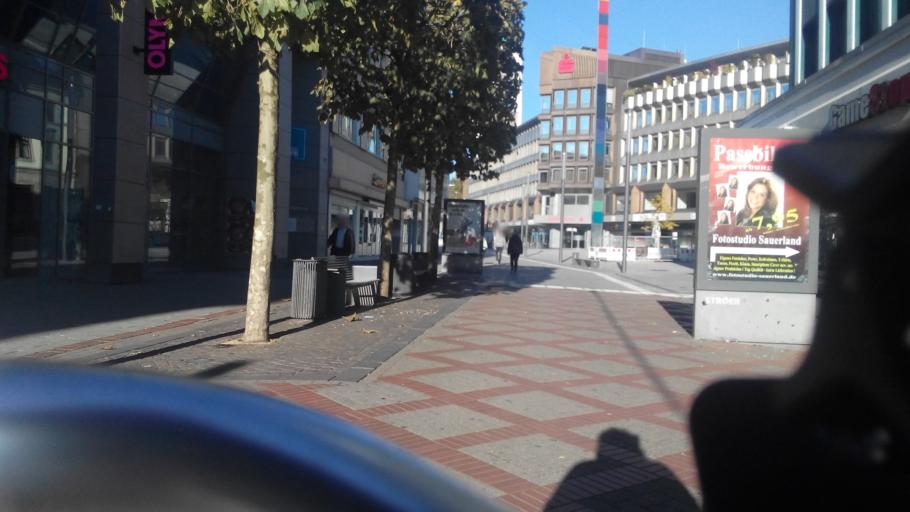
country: DE
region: North Rhine-Westphalia
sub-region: Regierungsbezirk Munster
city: Gelsenkirchen
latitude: 51.5091
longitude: 7.0968
